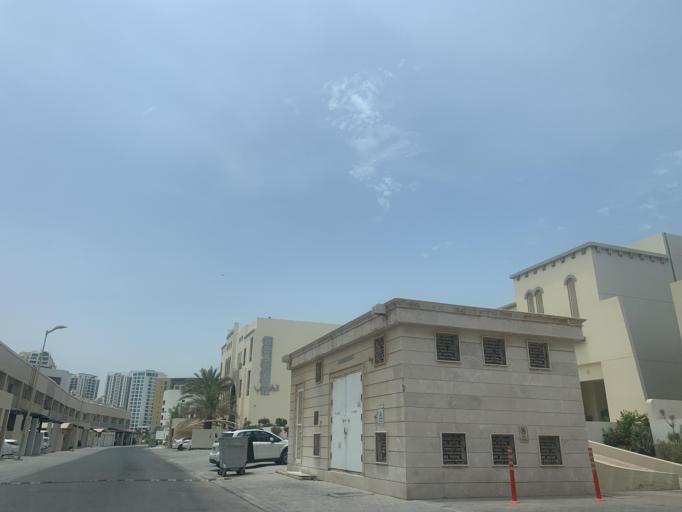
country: BH
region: Muharraq
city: Al Hadd
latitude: 26.2932
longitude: 50.6692
